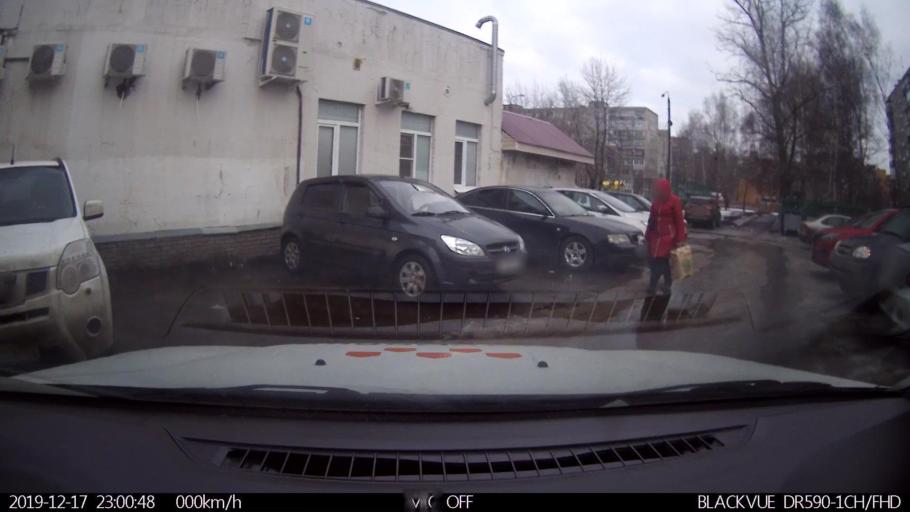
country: RU
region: Nizjnij Novgorod
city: Neklyudovo
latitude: 56.3547
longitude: 43.8576
